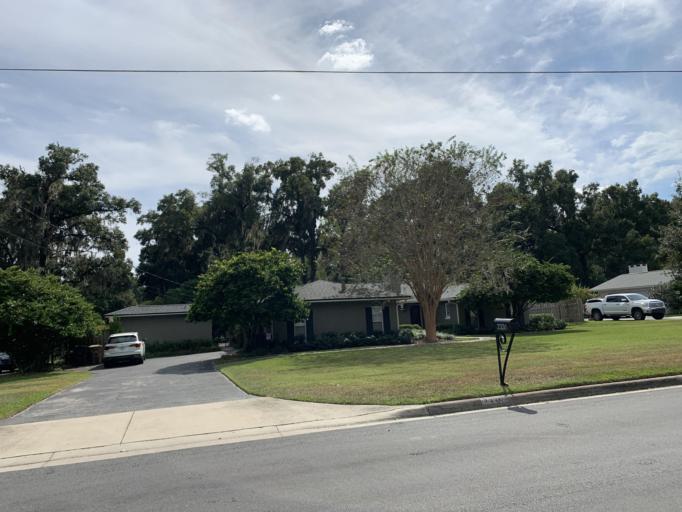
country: US
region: Florida
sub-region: Marion County
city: Ocala
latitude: 29.1768
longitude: -82.1052
